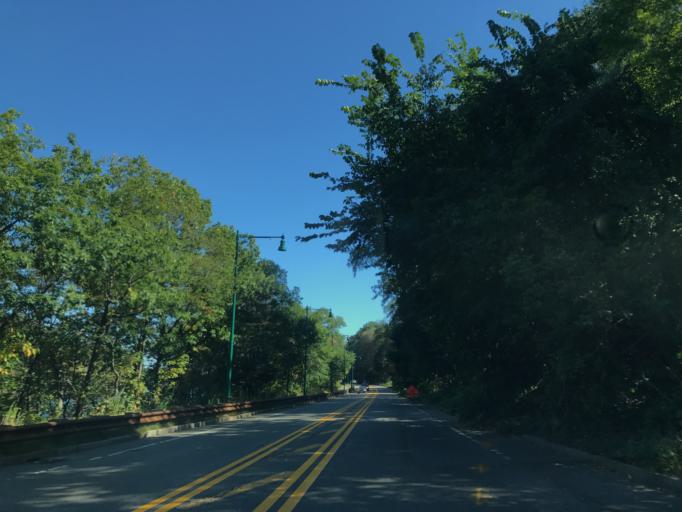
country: US
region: Massachusetts
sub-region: Middlesex County
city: Watertown
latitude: 42.3596
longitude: -71.1803
